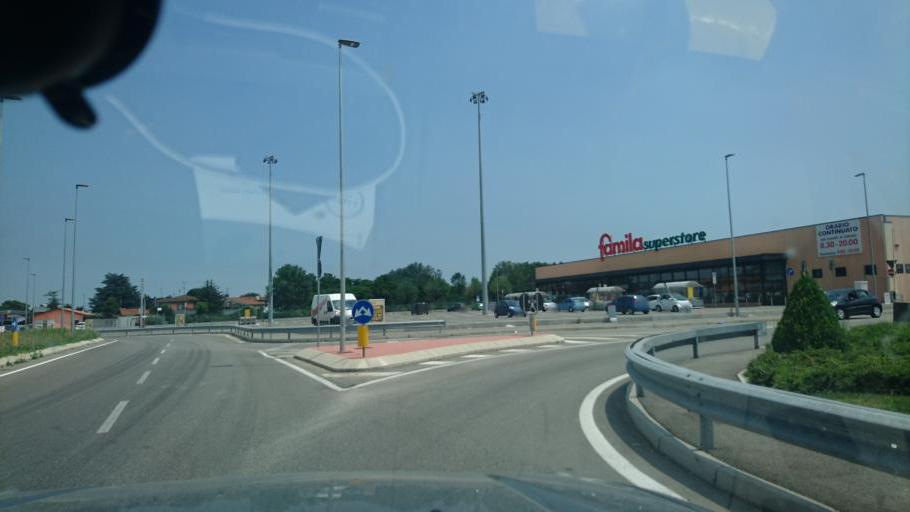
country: IT
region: Veneto
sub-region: Provincia di Padova
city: Monselice
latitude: 45.2303
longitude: 11.7485
